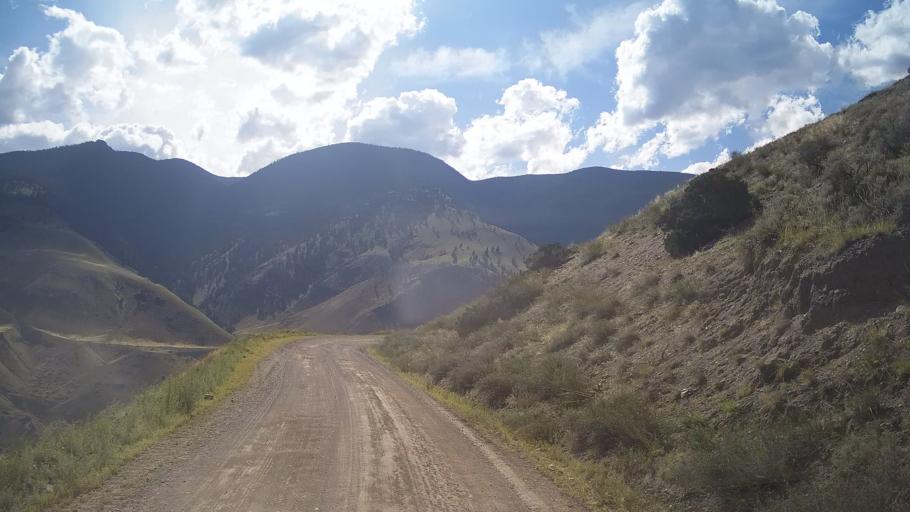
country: CA
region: British Columbia
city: Lillooet
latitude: 51.1827
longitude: -122.1180
